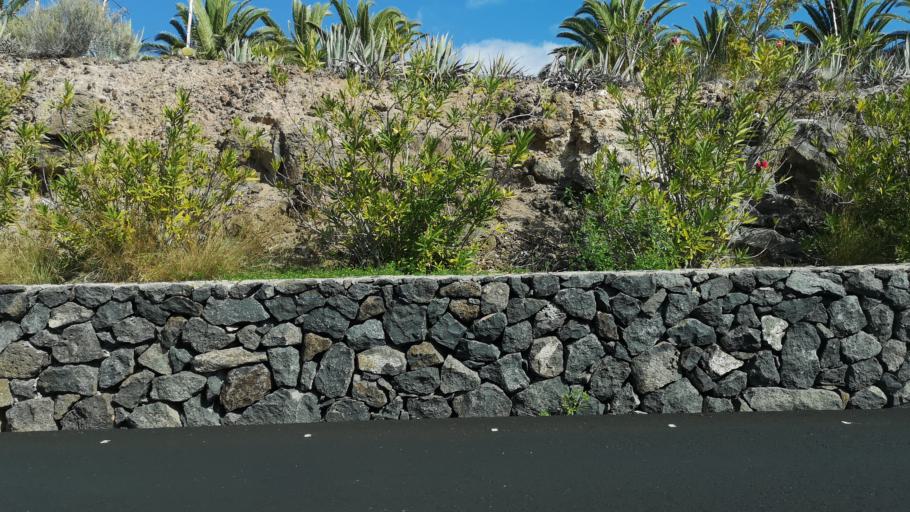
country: ES
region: Canary Islands
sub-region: Provincia de Santa Cruz de Tenerife
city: Alajero
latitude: 28.0385
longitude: -17.1953
